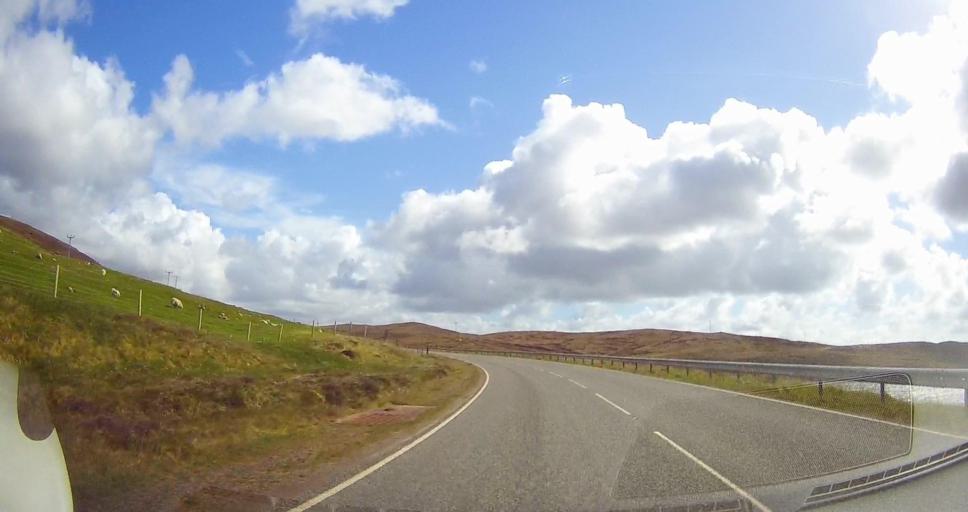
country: GB
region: Scotland
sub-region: Shetland Islands
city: Lerwick
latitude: 60.4638
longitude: -1.4047
